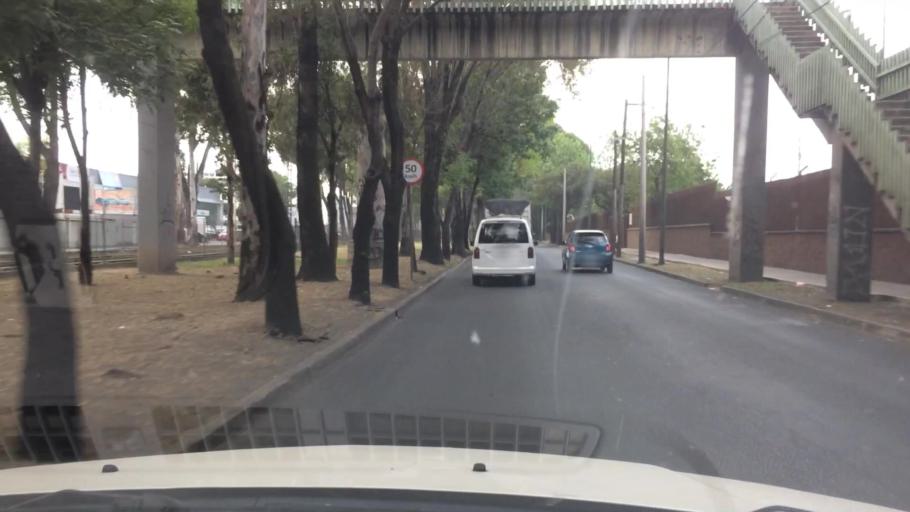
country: MX
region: Mexico City
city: Tlalpan
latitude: 19.2845
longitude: -99.1415
